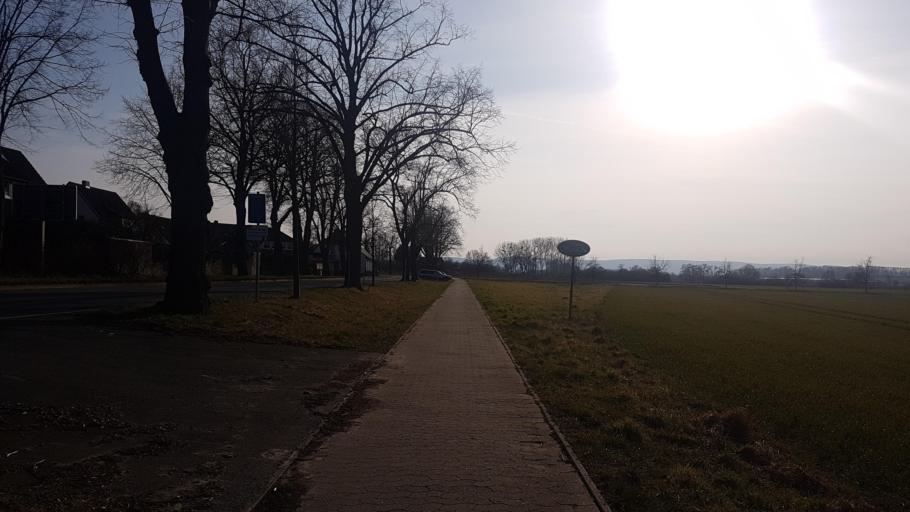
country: DE
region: Lower Saxony
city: Ronnenberg
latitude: 52.3089
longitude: 9.6787
